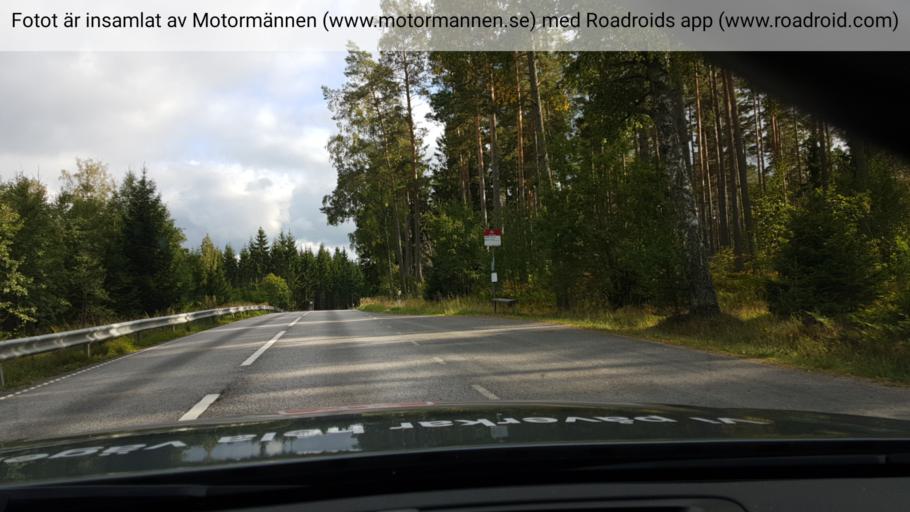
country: SE
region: Stockholm
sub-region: Norrtalje Kommun
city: Hallstavik
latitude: 59.9928
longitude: 18.5899
